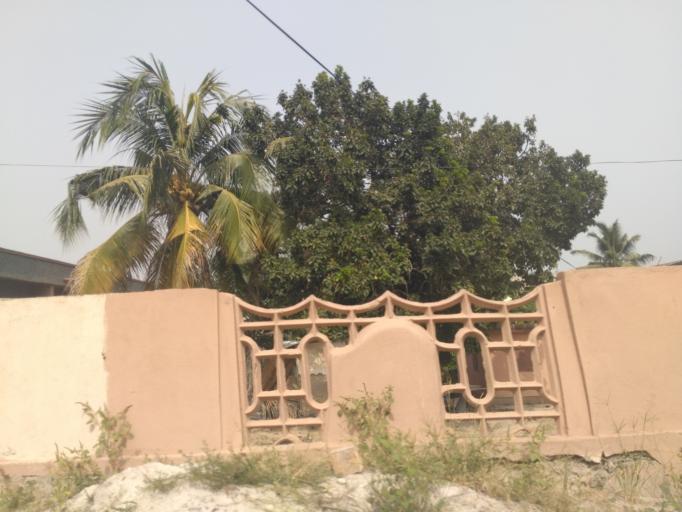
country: GH
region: Ashanti
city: Kumasi
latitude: 6.6757
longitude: -1.6017
